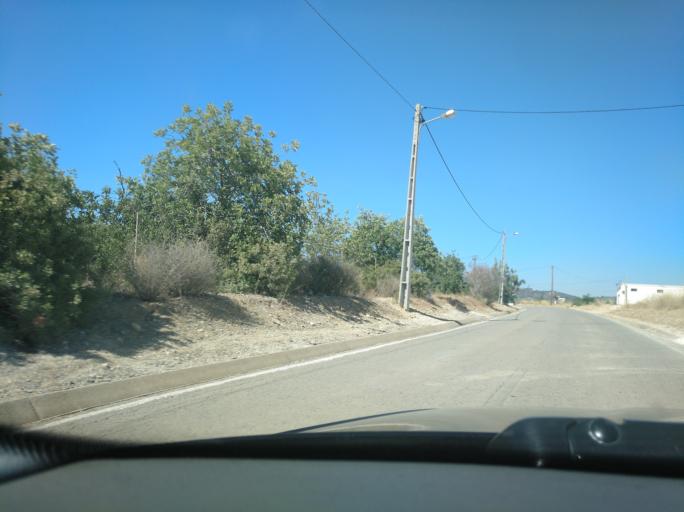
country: PT
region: Faro
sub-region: Faro
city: Faro
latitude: 37.0684
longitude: -7.8956
